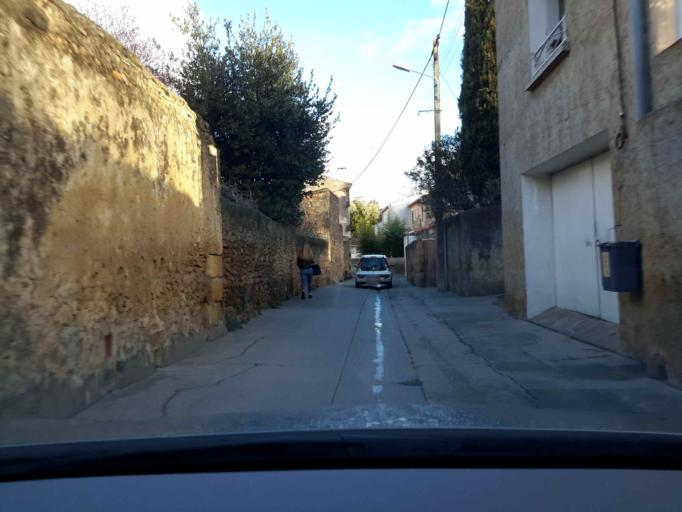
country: FR
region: Languedoc-Roussillon
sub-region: Departement du Gard
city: Beauvoisin
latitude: 43.7188
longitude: 4.3247
